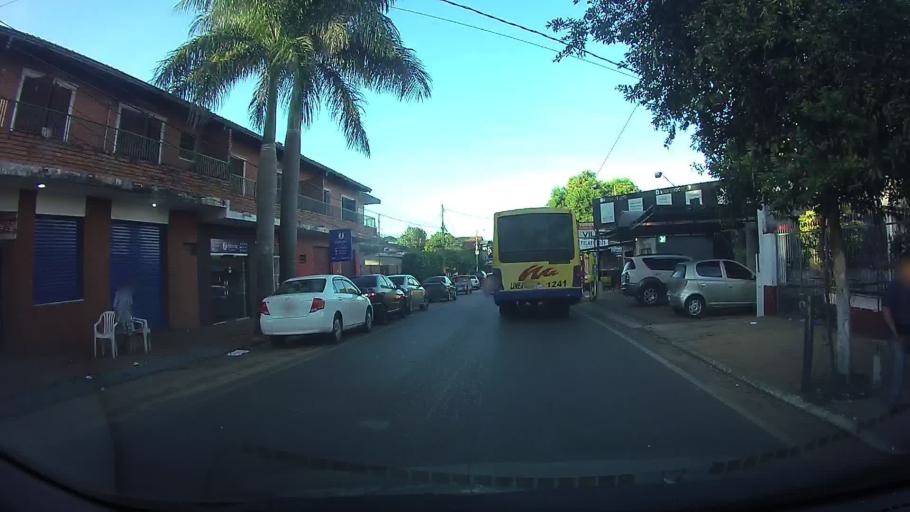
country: PY
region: Central
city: San Lorenzo
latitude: -25.2722
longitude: -57.4979
